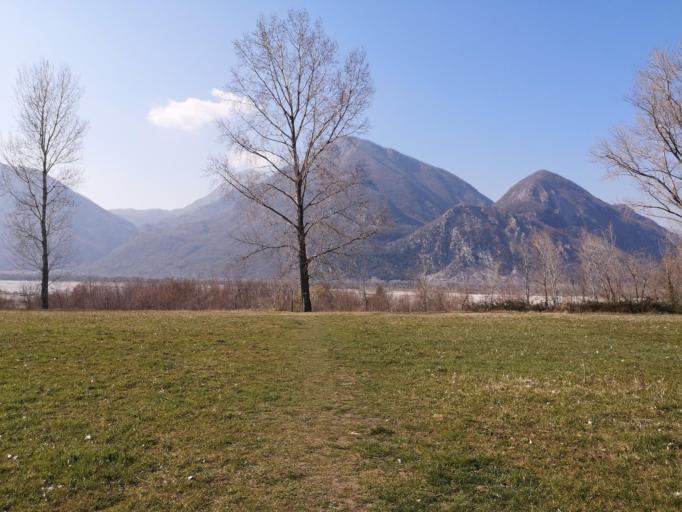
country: IT
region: Friuli Venezia Giulia
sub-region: Provincia di Udine
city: Osoppo
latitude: 46.2620
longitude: 13.0737
